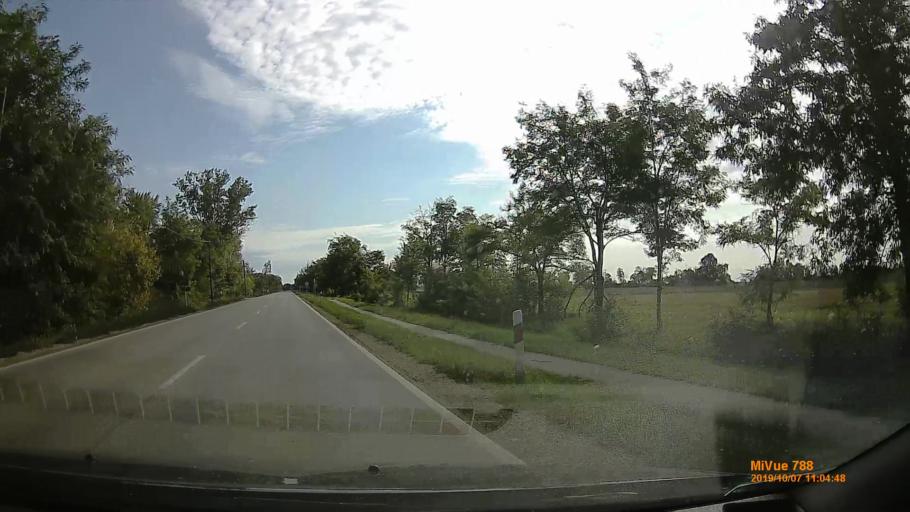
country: HU
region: Bekes
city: Kondoros
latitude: 46.7527
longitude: 20.8251
